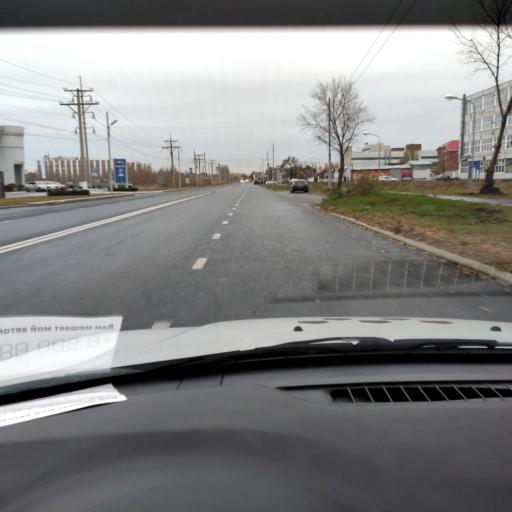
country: RU
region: Samara
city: Tol'yatti
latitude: 53.5537
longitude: 49.2933
